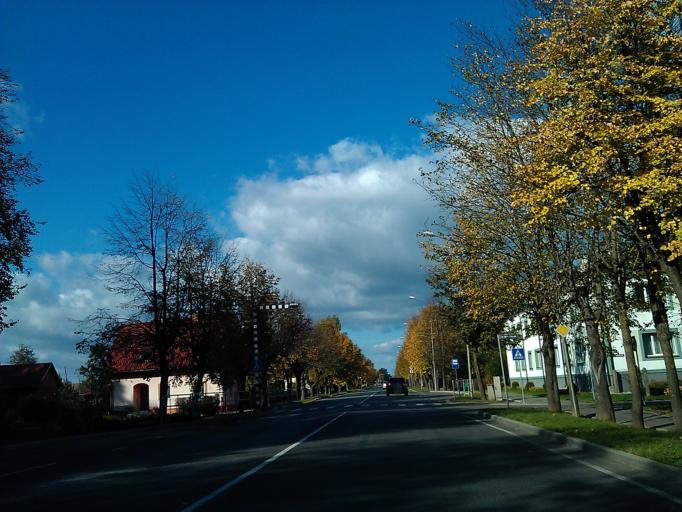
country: LV
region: Livani
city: Livani
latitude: 56.3630
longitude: 26.1711
